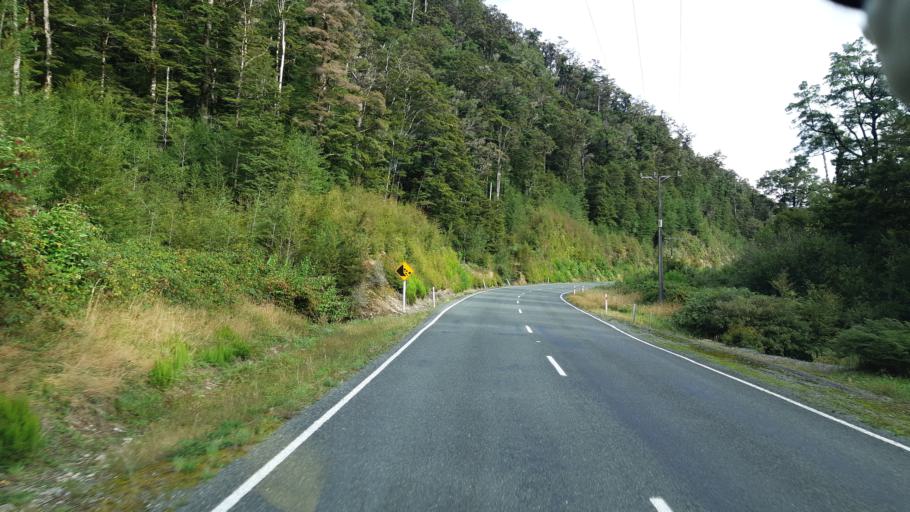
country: NZ
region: West Coast
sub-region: Buller District
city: Westport
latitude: -41.9972
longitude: 172.2237
